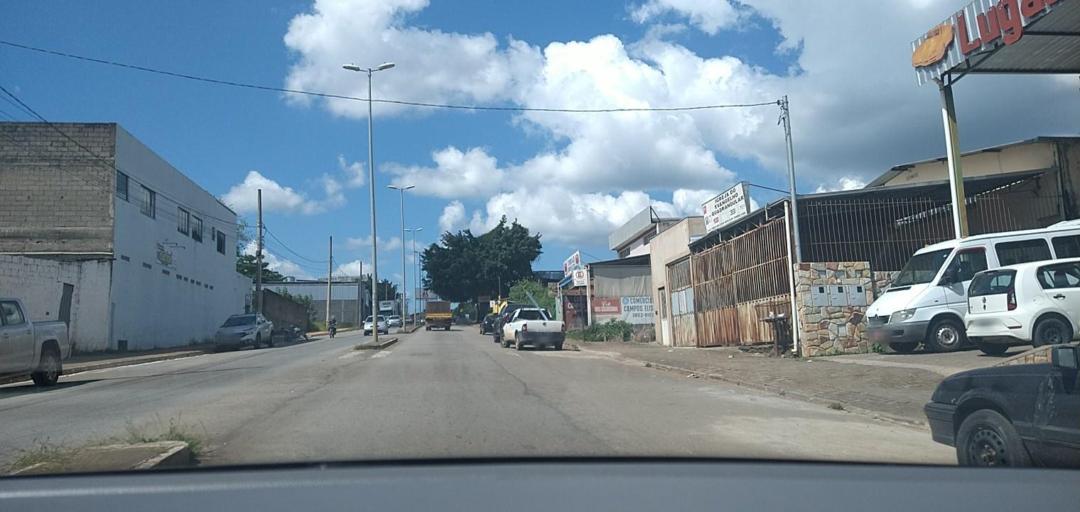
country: BR
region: Minas Gerais
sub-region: Joao Monlevade
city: Joao Monlevade
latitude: -19.8356
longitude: -43.1911
